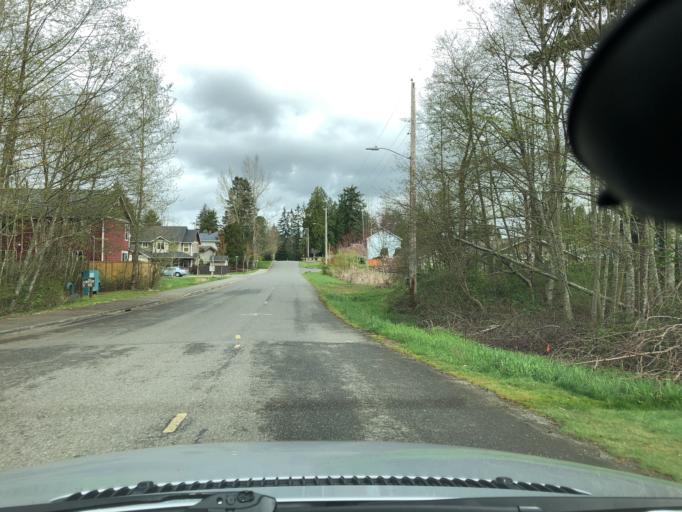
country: US
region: Washington
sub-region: Whatcom County
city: Blaine
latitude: 48.9772
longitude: -122.7352
